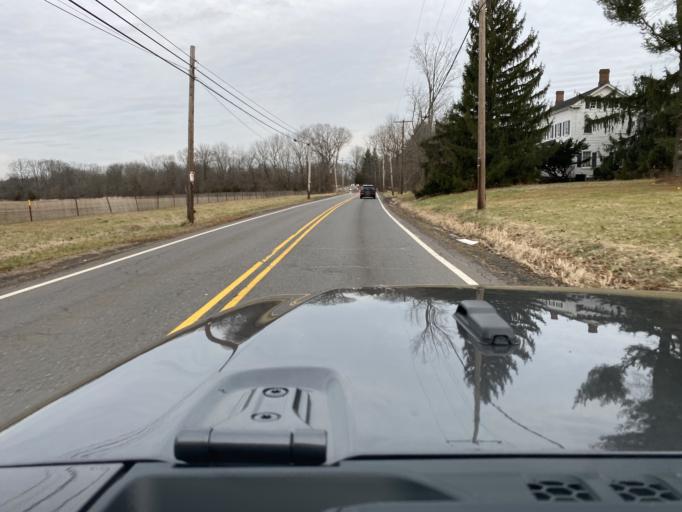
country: US
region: New Jersey
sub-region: Somerset County
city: Bloomingdale
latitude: 40.5012
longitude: -74.7073
